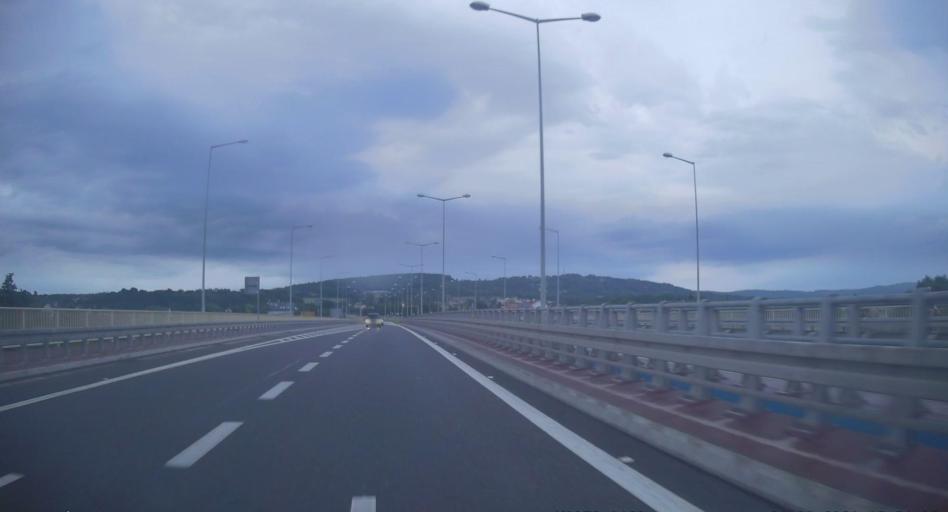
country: PL
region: Subcarpathian Voivodeship
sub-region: Powiat debicki
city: Pilzno
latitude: 49.9881
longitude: 21.3096
